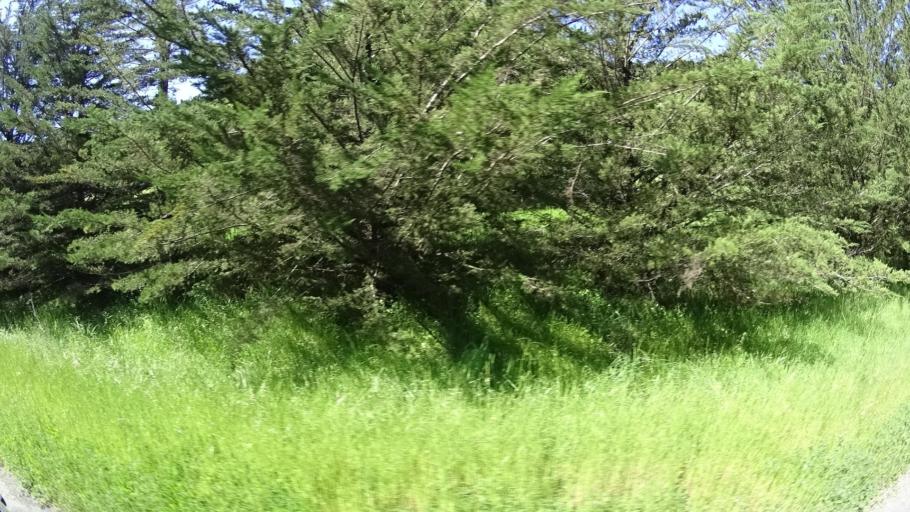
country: US
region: California
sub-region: Humboldt County
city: Rio Dell
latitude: 40.2352
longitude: -124.1178
